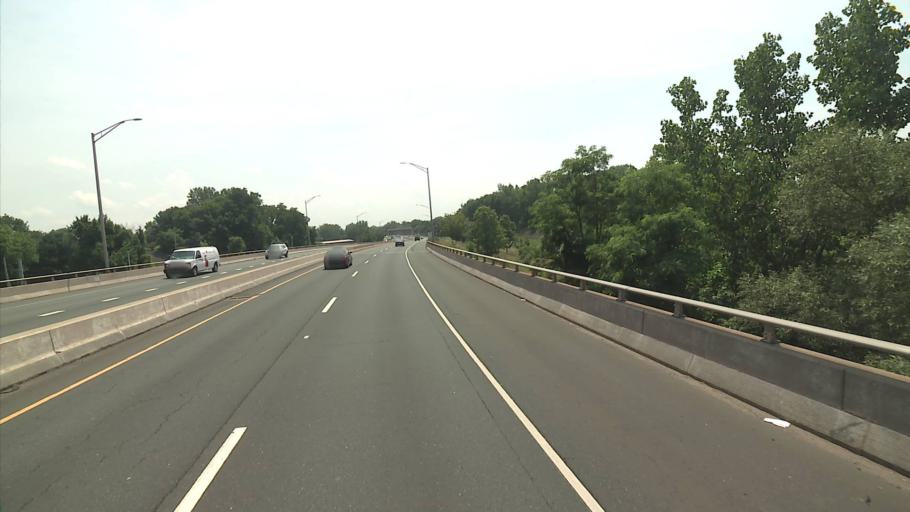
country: US
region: Connecticut
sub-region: Hartford County
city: South Windsor
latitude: 41.8176
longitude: -72.6561
